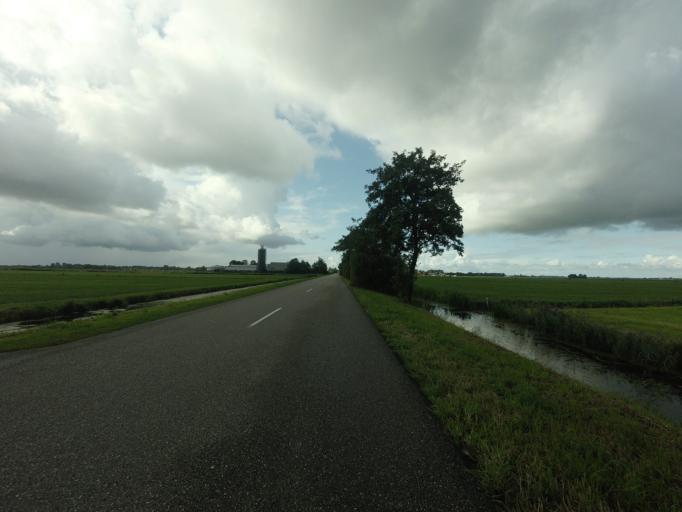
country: NL
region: Friesland
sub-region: Gemeente Boarnsterhim
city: Warten
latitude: 53.1561
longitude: 5.9137
